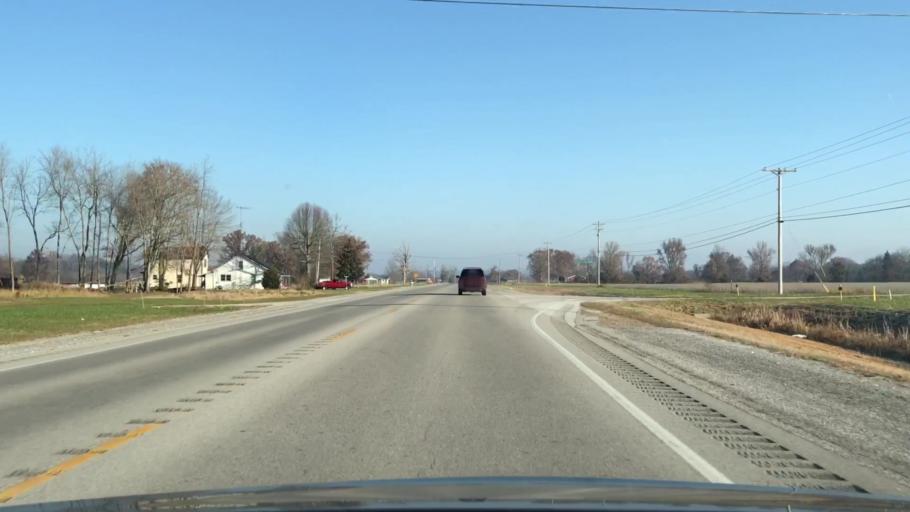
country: US
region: Kentucky
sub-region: Edmonson County
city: Brownsville
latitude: 37.1358
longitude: -86.2322
